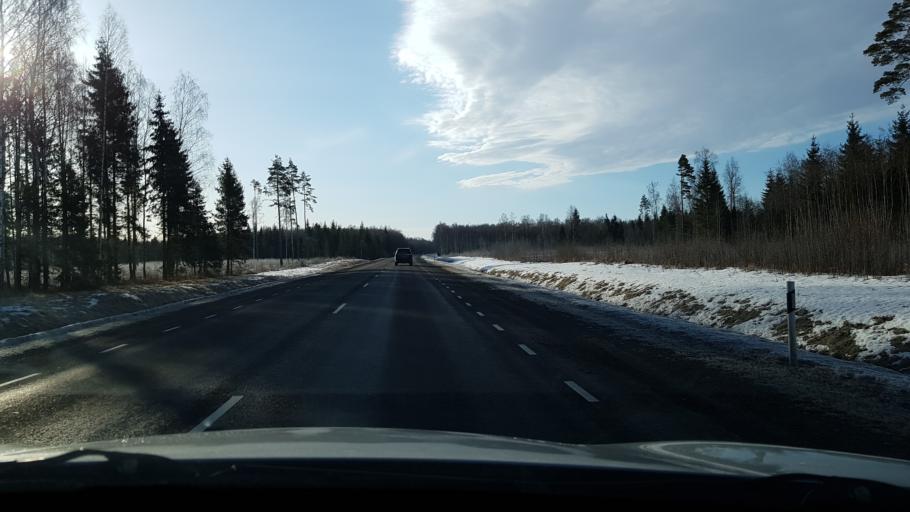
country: EE
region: Viljandimaa
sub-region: Vohma linn
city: Vohma
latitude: 58.6083
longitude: 25.5721
